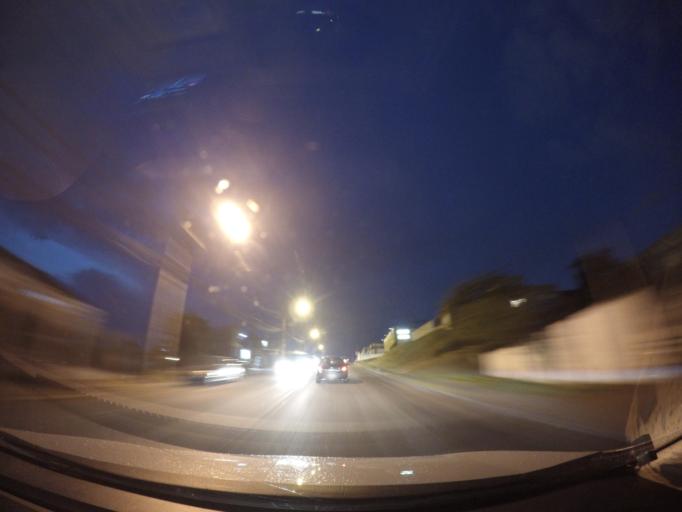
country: BR
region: Parana
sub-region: Curitiba
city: Curitiba
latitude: -25.4641
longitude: -49.2654
